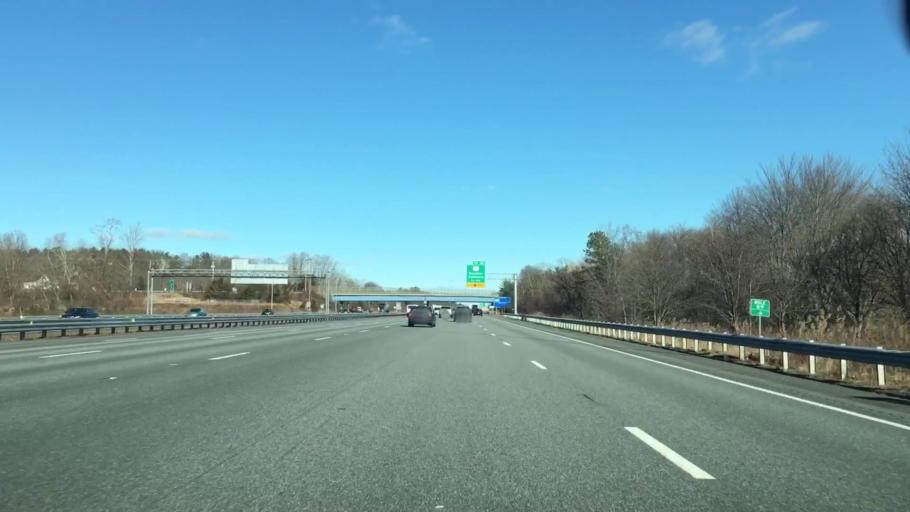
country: US
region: New Hampshire
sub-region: Rockingham County
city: Seabrook
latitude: 42.8645
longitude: -70.8920
